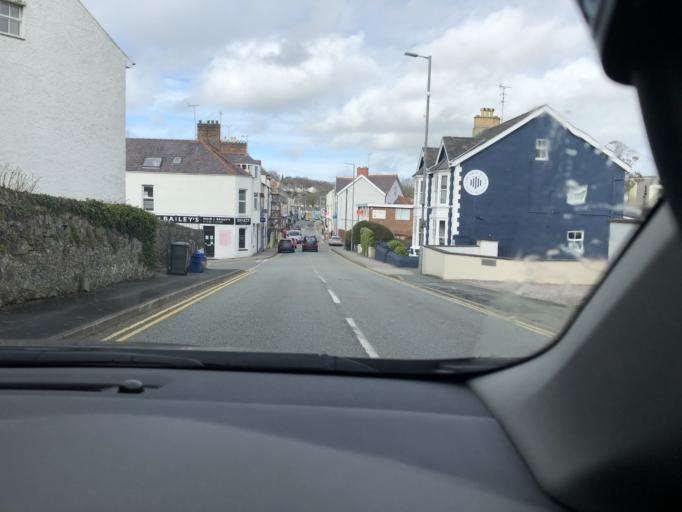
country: GB
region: Wales
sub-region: Anglesey
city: Menai Bridge
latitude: 53.2248
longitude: -4.1633
